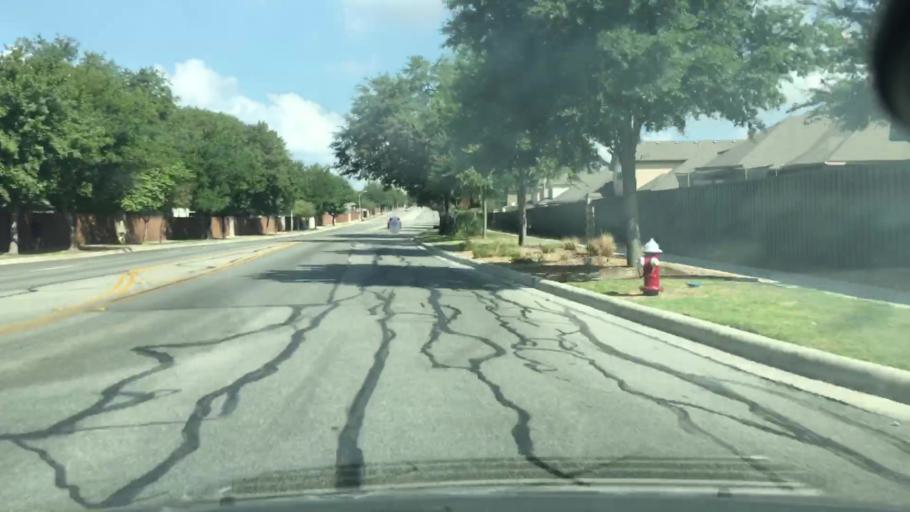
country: US
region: Texas
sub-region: Guadalupe County
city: Cibolo
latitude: 29.5769
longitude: -98.2437
